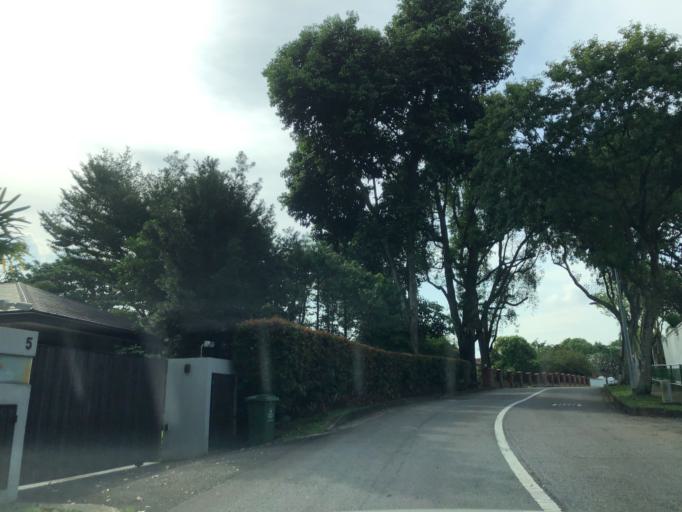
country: SG
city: Singapore
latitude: 1.3102
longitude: 103.8238
